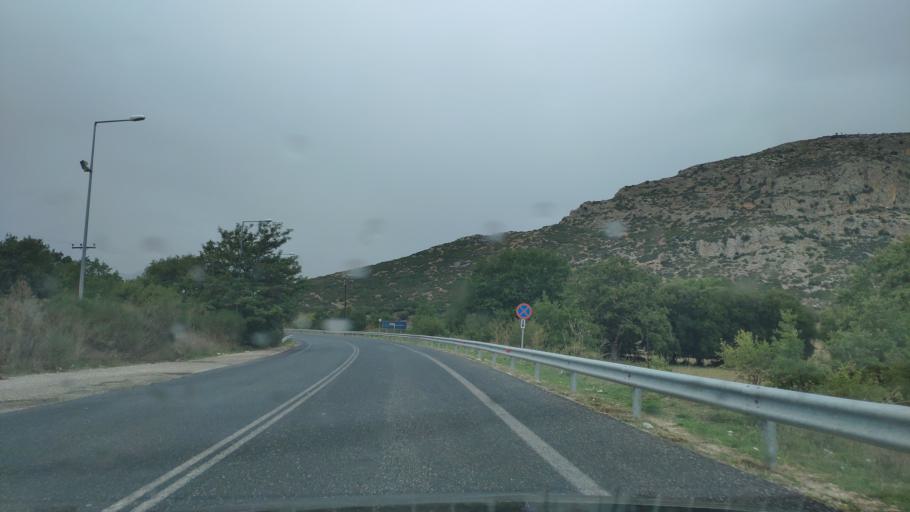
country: GR
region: Peloponnese
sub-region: Nomos Arkadias
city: Tripoli
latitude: 37.5941
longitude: 22.4346
